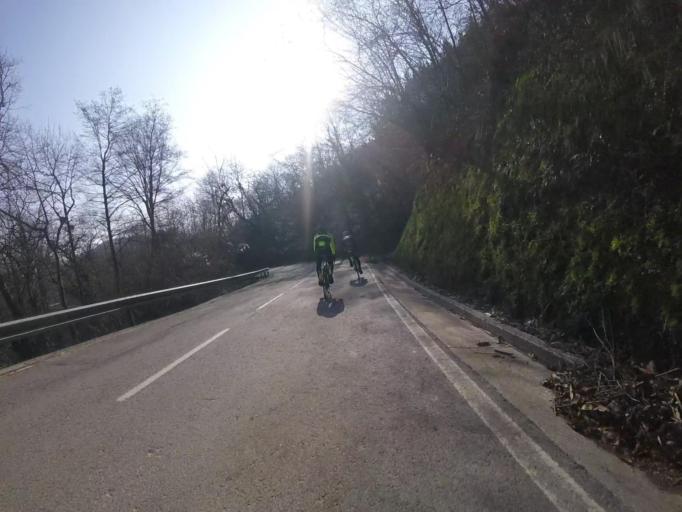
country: ES
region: Navarre
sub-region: Provincia de Navarra
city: Bera
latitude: 43.2907
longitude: -1.6868
